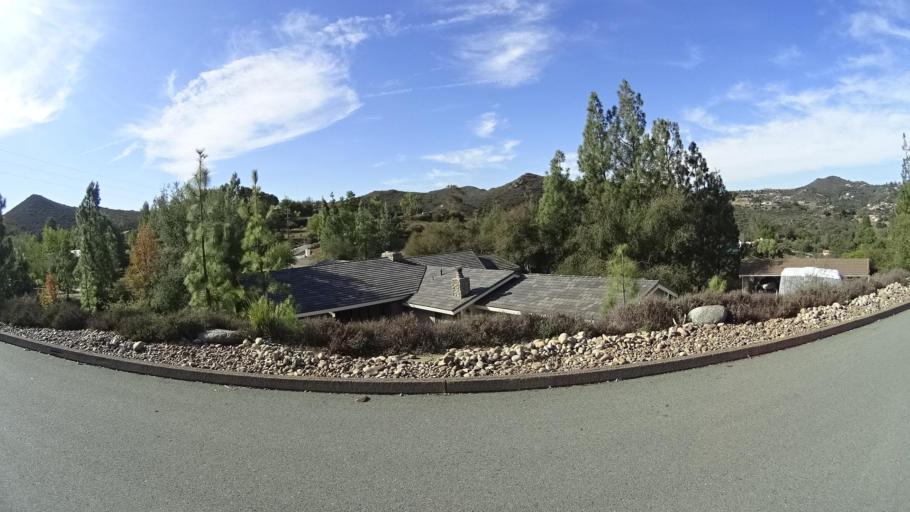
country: US
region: California
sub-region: San Diego County
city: Alpine
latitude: 32.8144
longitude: -116.7325
